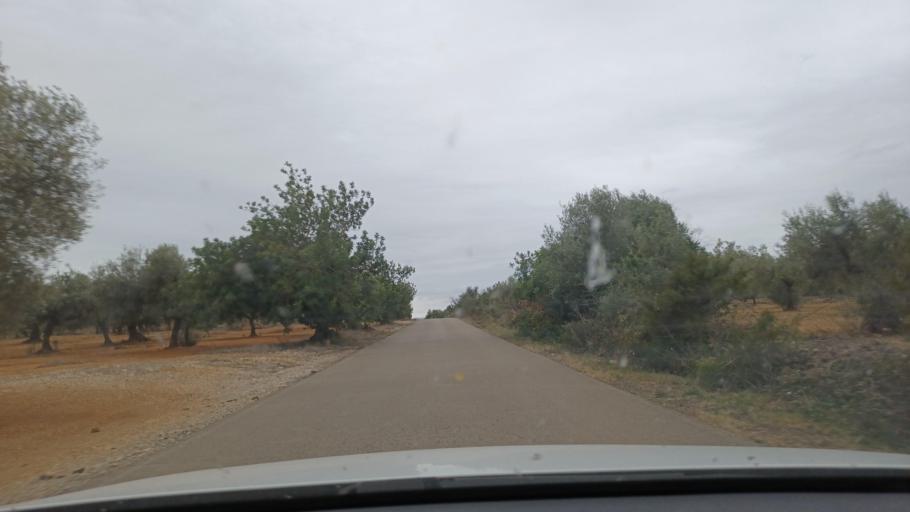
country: ES
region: Valencia
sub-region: Provincia de Castello
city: Canet lo Roig
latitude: 40.5742
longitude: 0.2790
